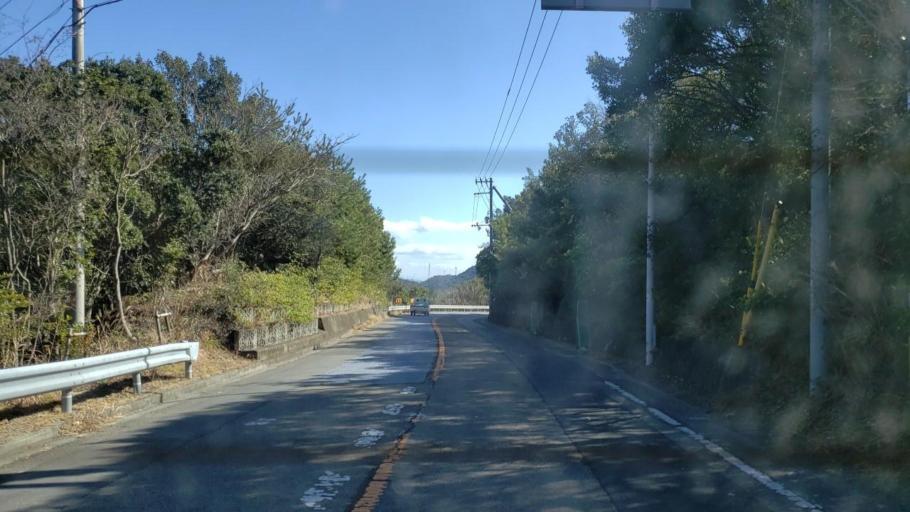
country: JP
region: Tokushima
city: Narutocho-mitsuishi
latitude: 34.2362
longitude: 134.6144
